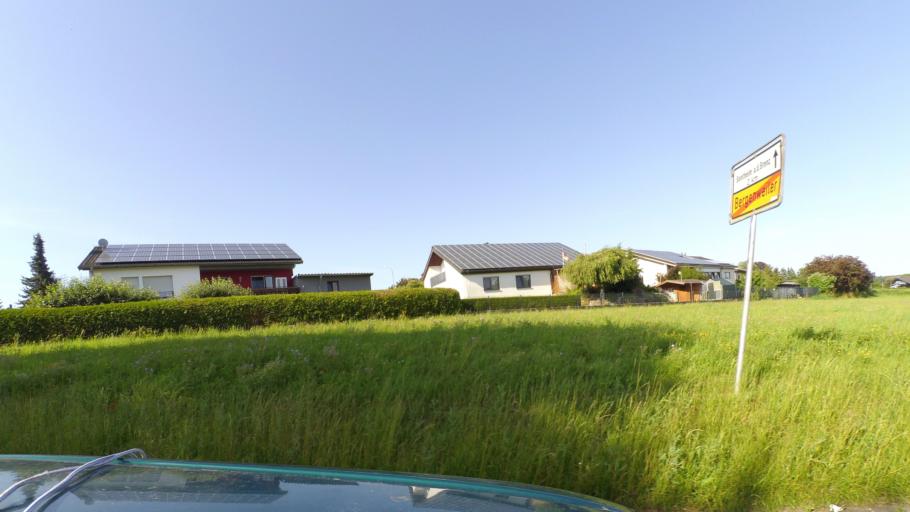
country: DE
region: Baden-Wuerttemberg
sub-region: Regierungsbezirk Stuttgart
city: Sontheim an der Brenz
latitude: 48.5706
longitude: 10.2750
